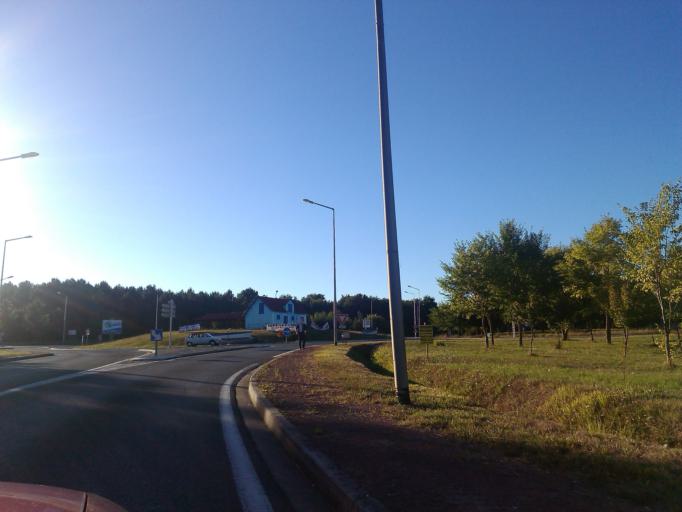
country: FR
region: Poitou-Charentes
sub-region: Departement de la Charente-Maritime
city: Chaillevette
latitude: 45.7207
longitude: -1.0789
